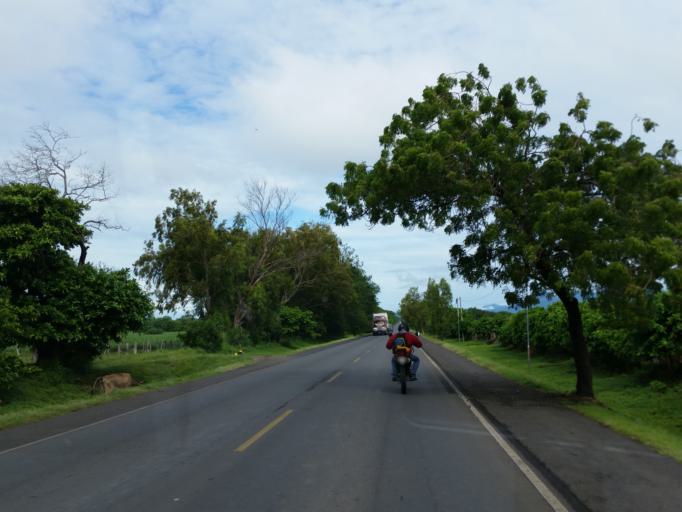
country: NI
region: Leon
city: Nagarote
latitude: 12.2852
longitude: -86.5833
